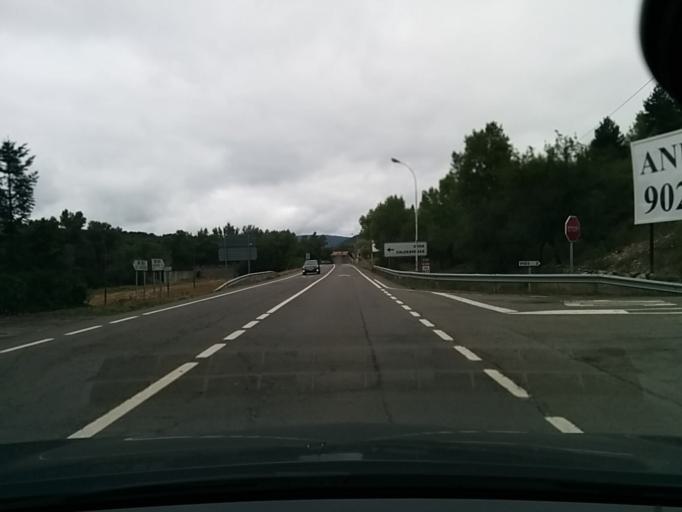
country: ES
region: Aragon
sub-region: Provincia de Huesca
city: Sabinanigo
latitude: 42.4399
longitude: -0.3952
